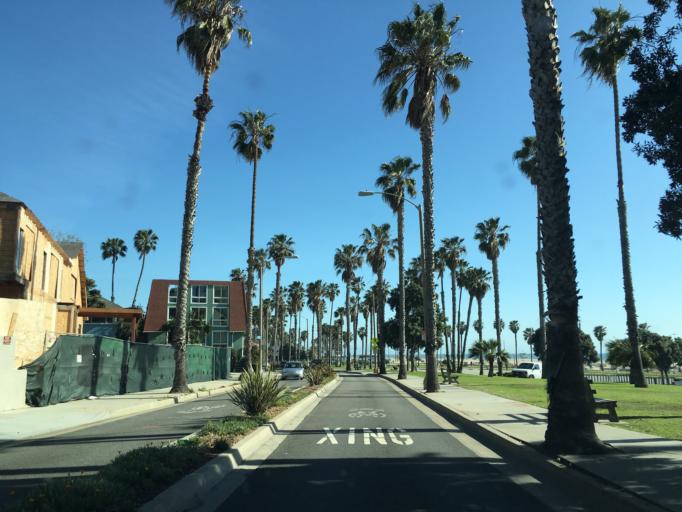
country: US
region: California
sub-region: Los Angeles County
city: Santa Monica
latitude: 34.0032
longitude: -118.4876
